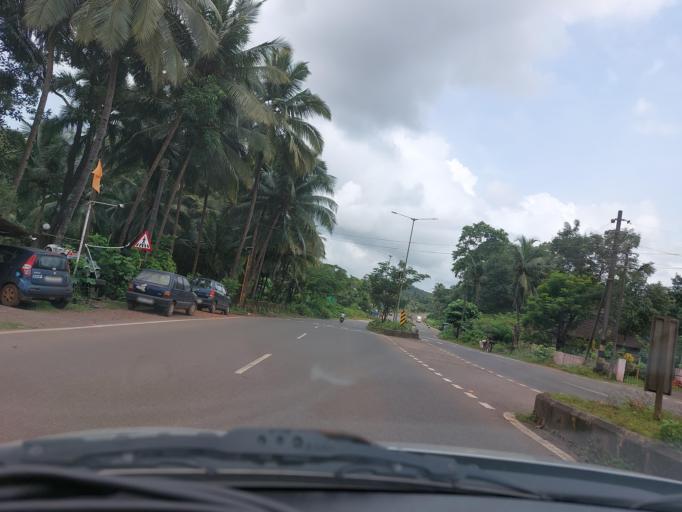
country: IN
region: Goa
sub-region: North Goa
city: Queula
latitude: 15.3871
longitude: 73.9994
